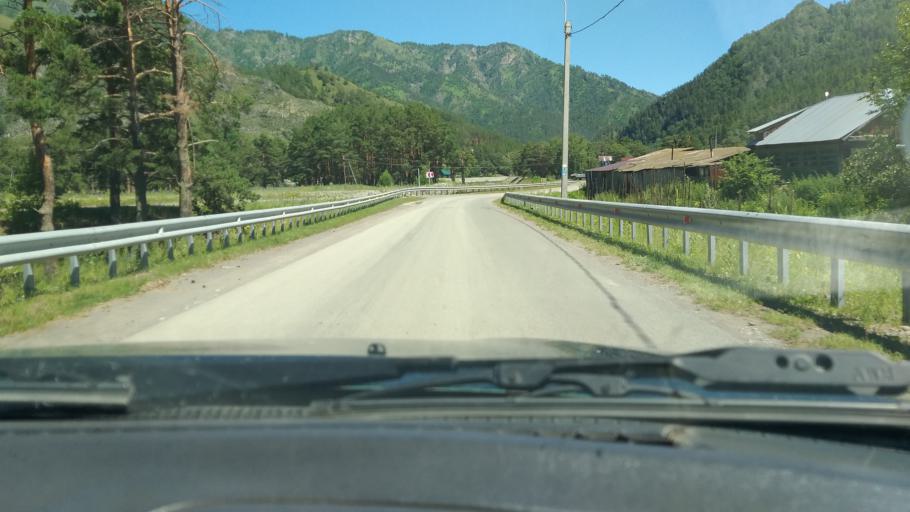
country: RU
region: Altay
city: Chemal
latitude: 51.3909
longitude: 86.0205
